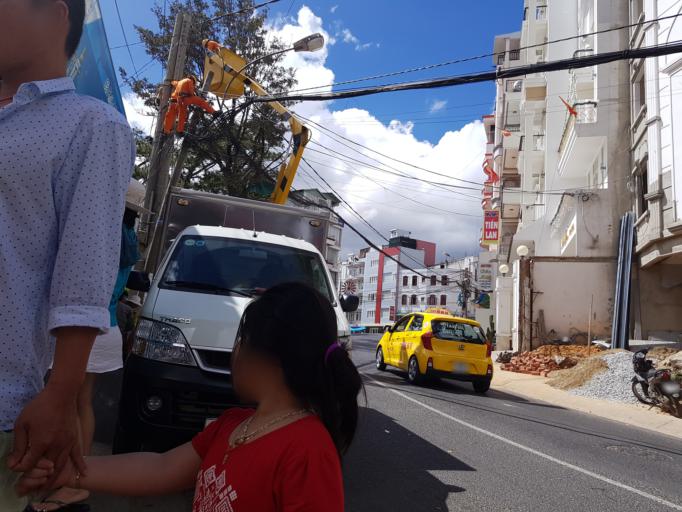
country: VN
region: Lam Dong
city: Da Lat
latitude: 11.9437
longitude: 108.4395
